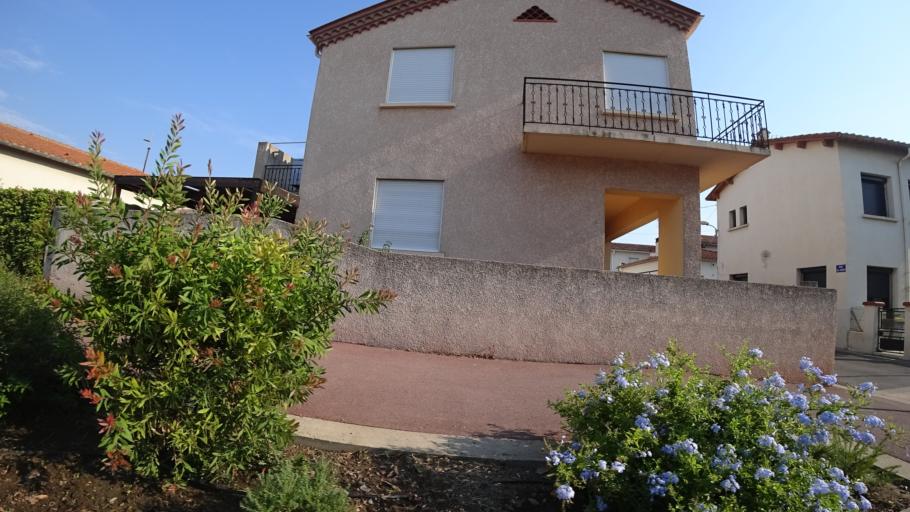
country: FR
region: Languedoc-Roussillon
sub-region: Departement des Pyrenees-Orientales
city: Villelongue-de-la-Salanque
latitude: 42.7266
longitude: 2.9806
